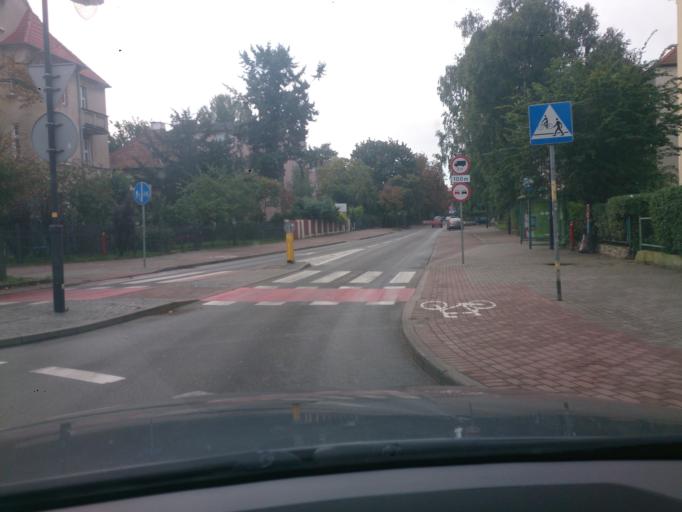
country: PL
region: Pomeranian Voivodeship
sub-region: Sopot
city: Sopot
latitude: 54.4417
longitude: 18.5567
